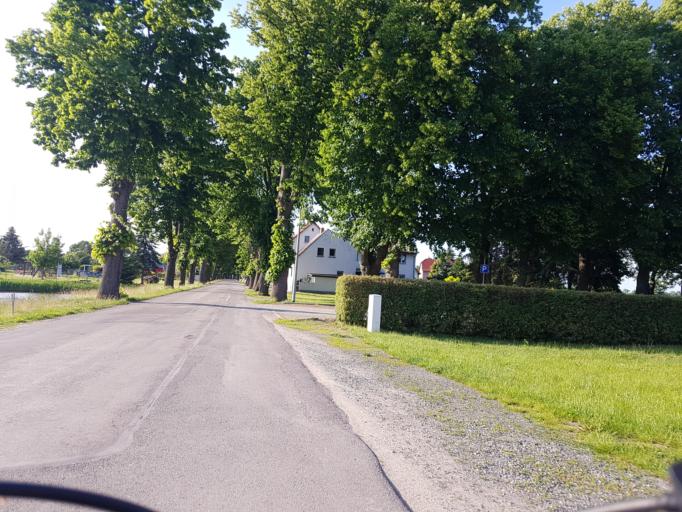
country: DE
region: Brandenburg
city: Elsterwerda
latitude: 51.4460
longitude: 13.5300
